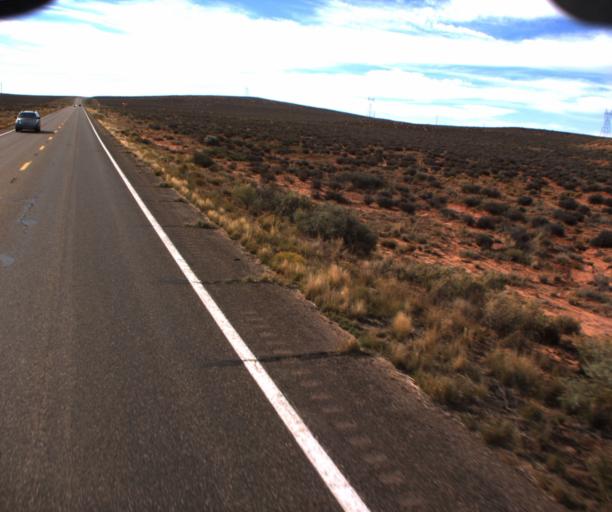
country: US
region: Arizona
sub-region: Coconino County
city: LeChee
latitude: 36.8240
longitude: -111.3088
